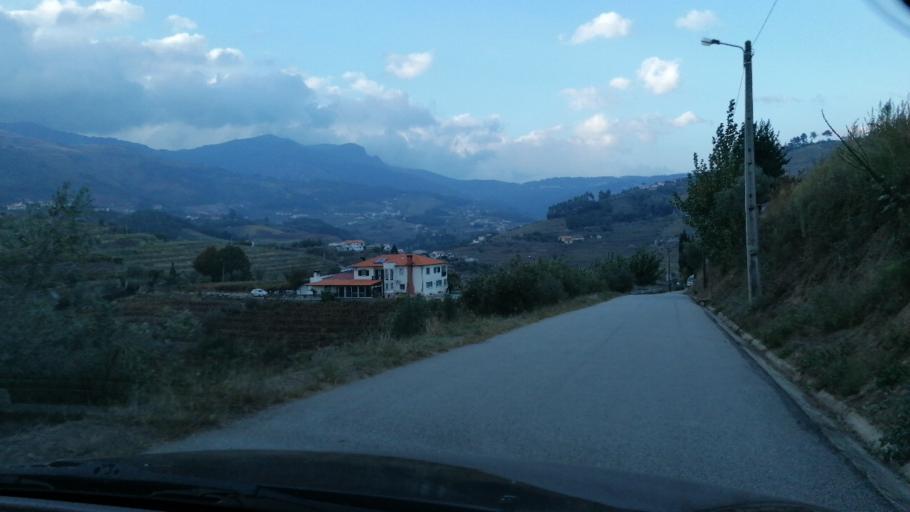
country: PT
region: Vila Real
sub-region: Mesao Frio
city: Mesao Frio
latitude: 41.1804
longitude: -7.8449
